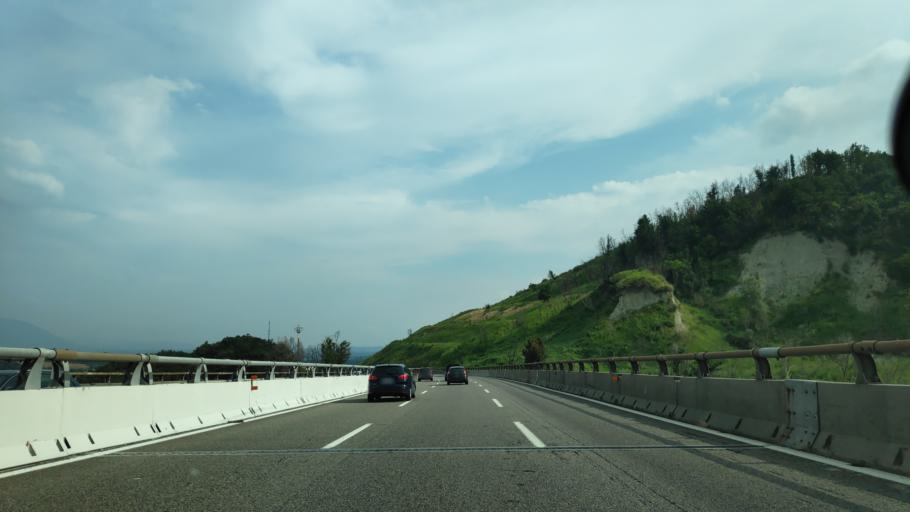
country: IT
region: Latium
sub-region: Citta metropolitana di Roma Capitale
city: Nazzano
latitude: 42.2115
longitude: 12.6011
